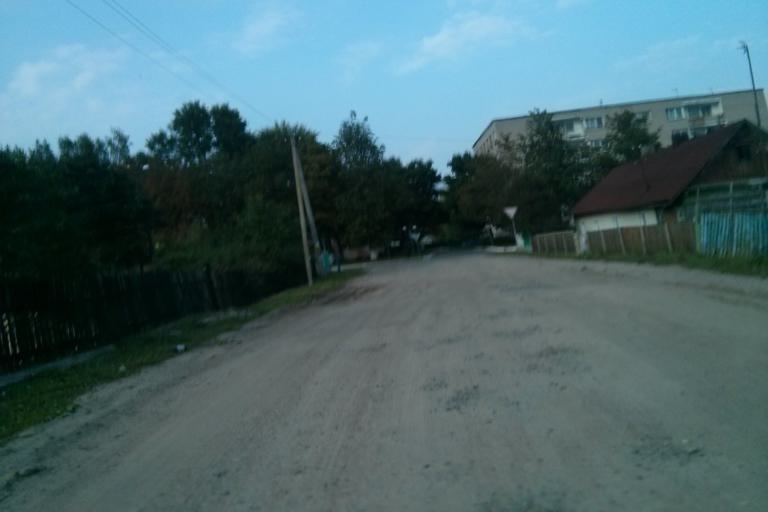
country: BY
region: Minsk
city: Chervyen'
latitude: 53.7172
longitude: 28.4049
